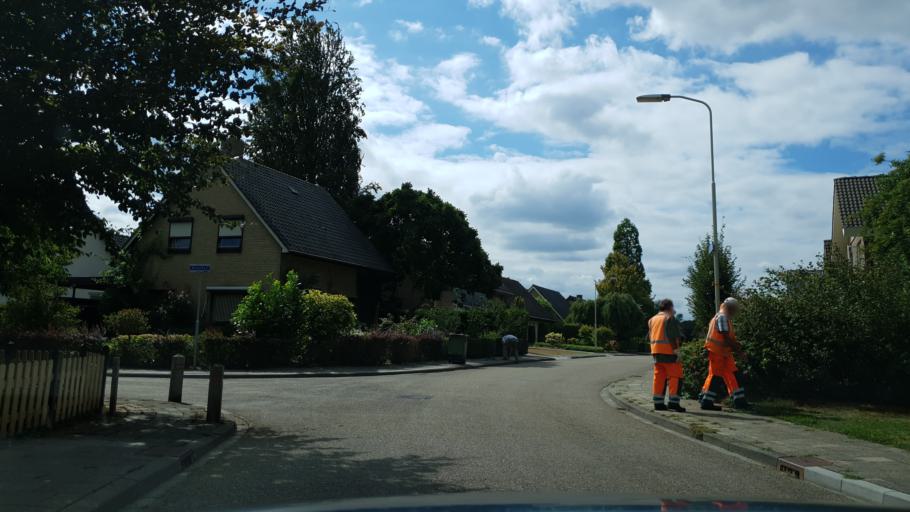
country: NL
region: North Brabant
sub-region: Gemeente Grave
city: Grave
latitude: 51.7581
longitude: 5.7854
